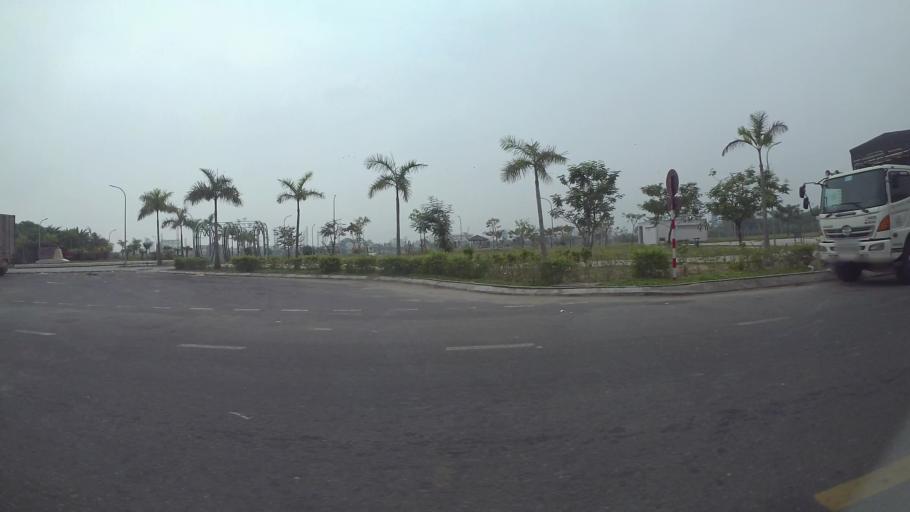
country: VN
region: Da Nang
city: Cam Le
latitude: 16.0281
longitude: 108.2192
